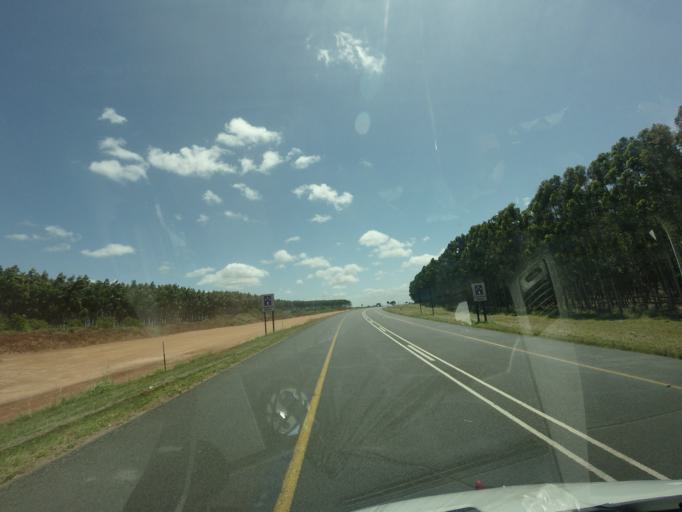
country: ZA
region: KwaZulu-Natal
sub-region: uThungulu District Municipality
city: Empangeni
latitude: -28.7374
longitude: 31.9399
